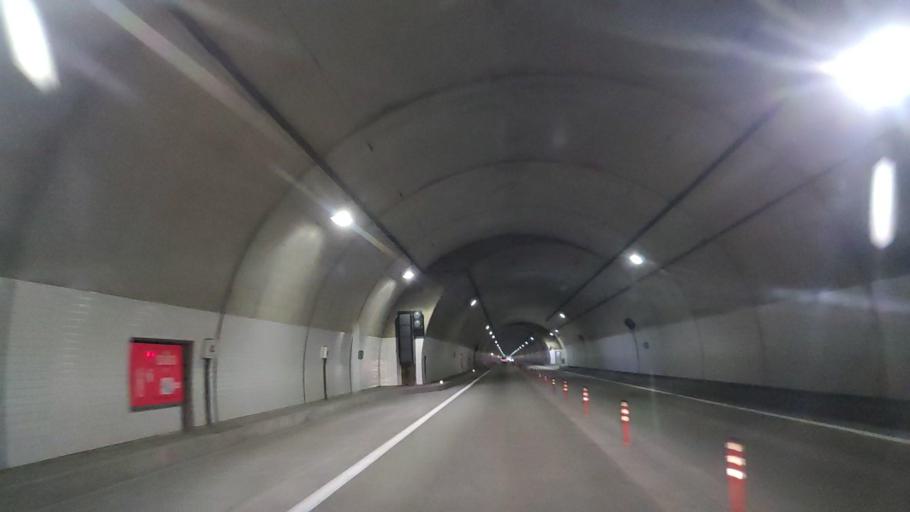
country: JP
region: Akita
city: Odate
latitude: 40.3504
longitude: 140.6763
